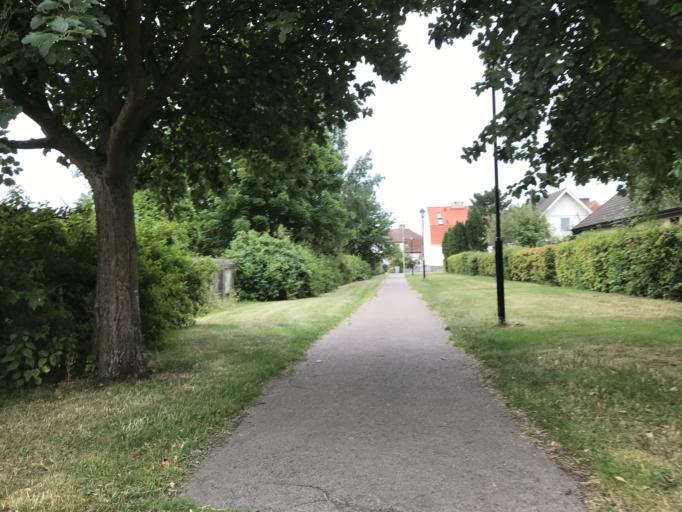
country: SE
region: Skane
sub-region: Landskrona
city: Landskrona
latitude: 55.8828
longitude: 12.8404
